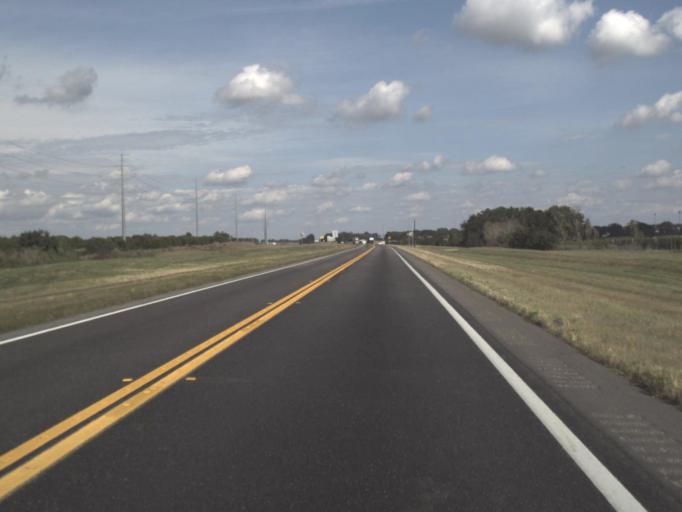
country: US
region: Florida
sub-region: Polk County
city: Fussels Corner
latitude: 28.0852
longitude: -81.8307
